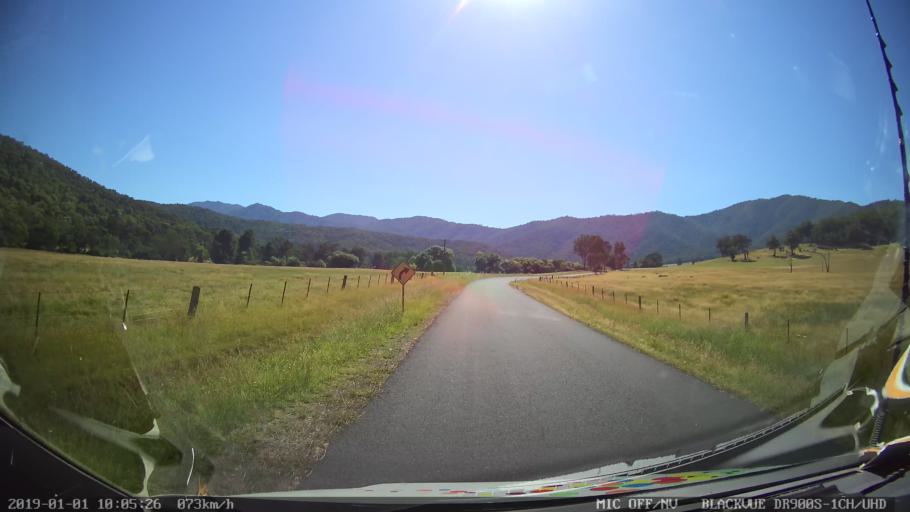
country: AU
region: New South Wales
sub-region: Snowy River
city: Jindabyne
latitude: -36.1737
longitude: 148.1356
